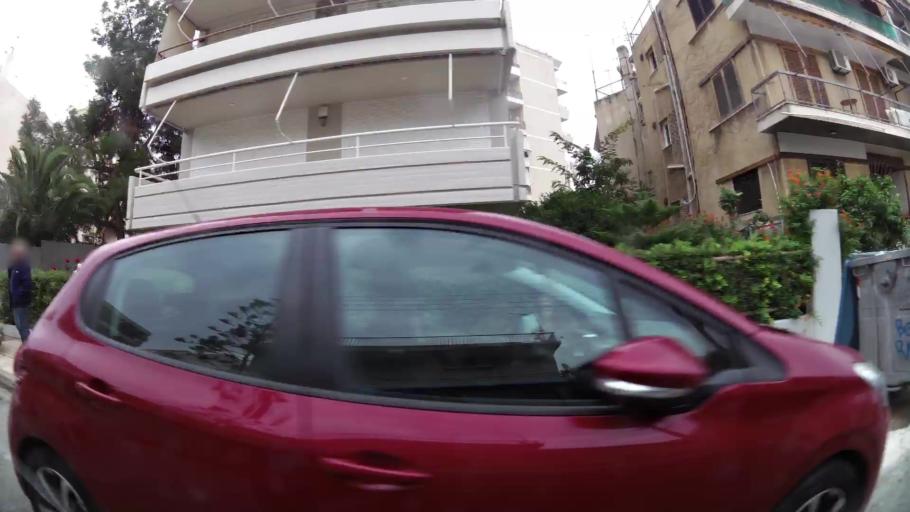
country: GR
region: Attica
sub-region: Nomarchia Athinas
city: Palaio Faliro
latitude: 37.9180
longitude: 23.7030
